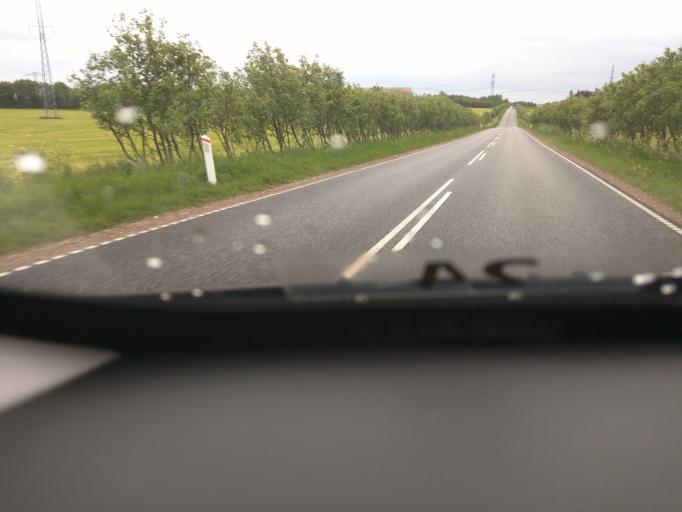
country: DK
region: Central Jutland
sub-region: Viborg Kommune
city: Bjerringbro
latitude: 56.4844
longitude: 9.5673
